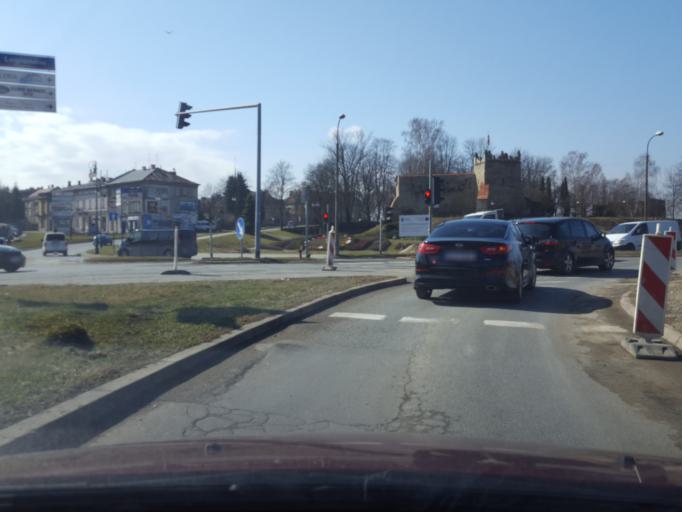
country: PL
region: Lesser Poland Voivodeship
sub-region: Powiat nowosadecki
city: Nowy Sacz
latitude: 49.6296
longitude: 20.6911
